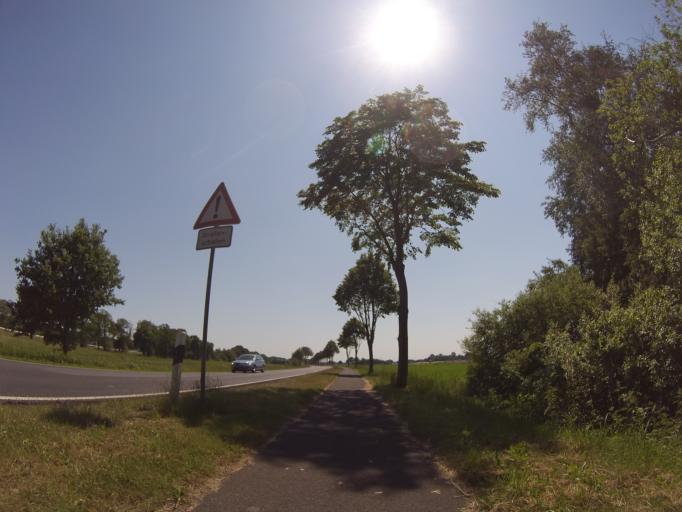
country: NL
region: Drenthe
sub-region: Gemeente Emmen
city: Schoonebeek
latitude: 52.6514
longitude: 6.8709
